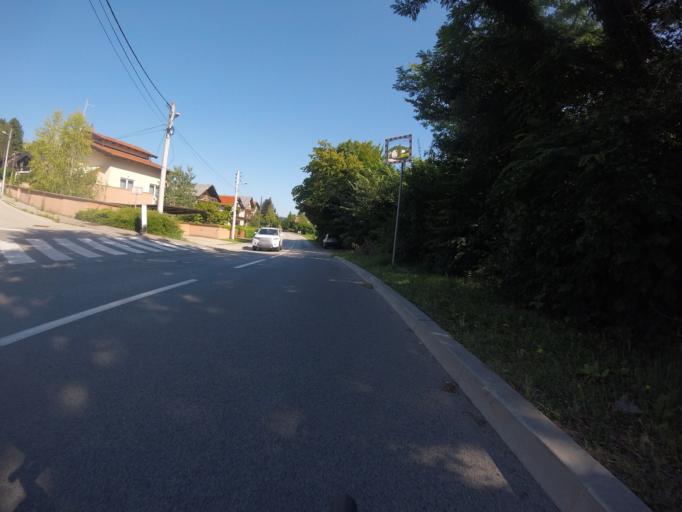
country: HR
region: Zagrebacka
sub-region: Grad Samobor
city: Samobor
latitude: 45.8161
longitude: 15.7045
